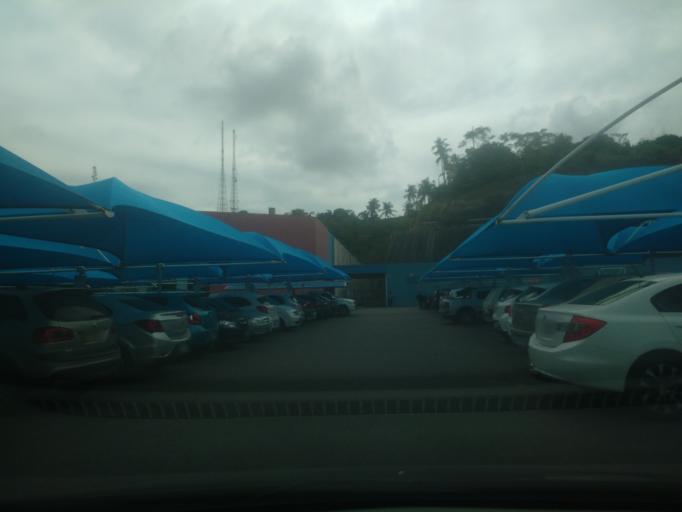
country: BR
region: Alagoas
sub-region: Maceio
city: Maceio
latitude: -9.6451
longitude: -35.7140
